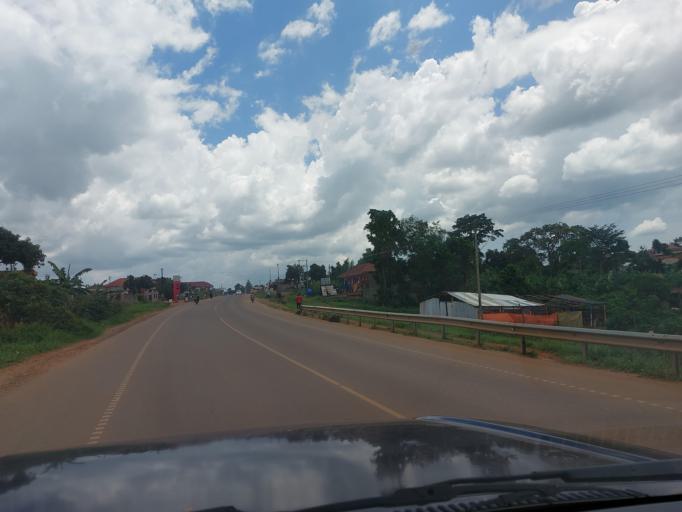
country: UG
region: Central Region
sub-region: Mukono District
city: Mukono
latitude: 0.3194
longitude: 32.7682
